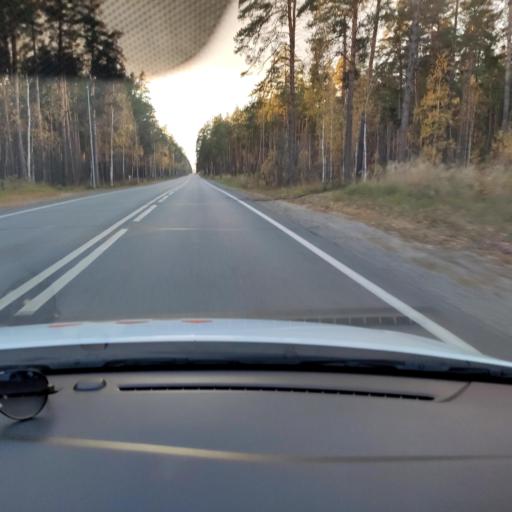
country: RU
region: Tatarstan
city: Stolbishchi
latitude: 55.6352
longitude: 49.0763
